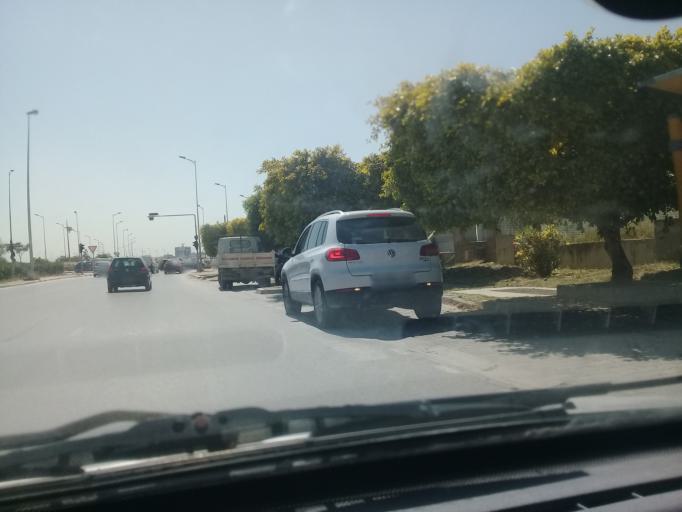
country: TN
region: Ariana
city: Ariana
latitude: 36.8318
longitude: 10.2178
